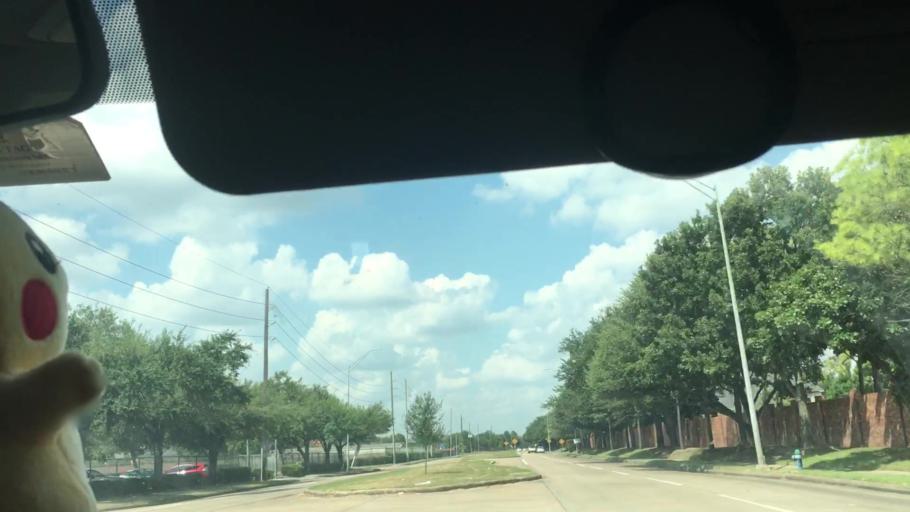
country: US
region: Texas
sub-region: Harris County
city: Bunker Hill Village
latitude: 29.7205
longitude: -95.5746
